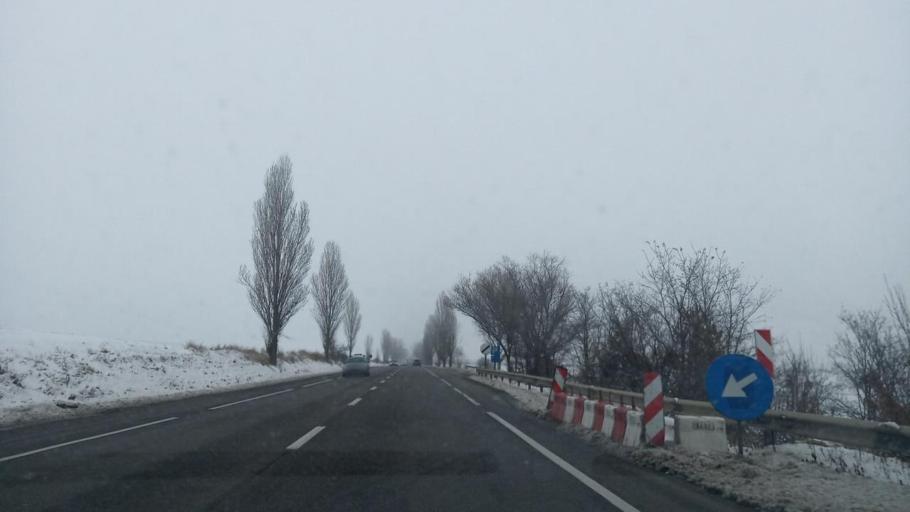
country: RO
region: Bacau
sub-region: Comuna Cleja
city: Somusca
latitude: 46.4131
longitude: 26.9372
